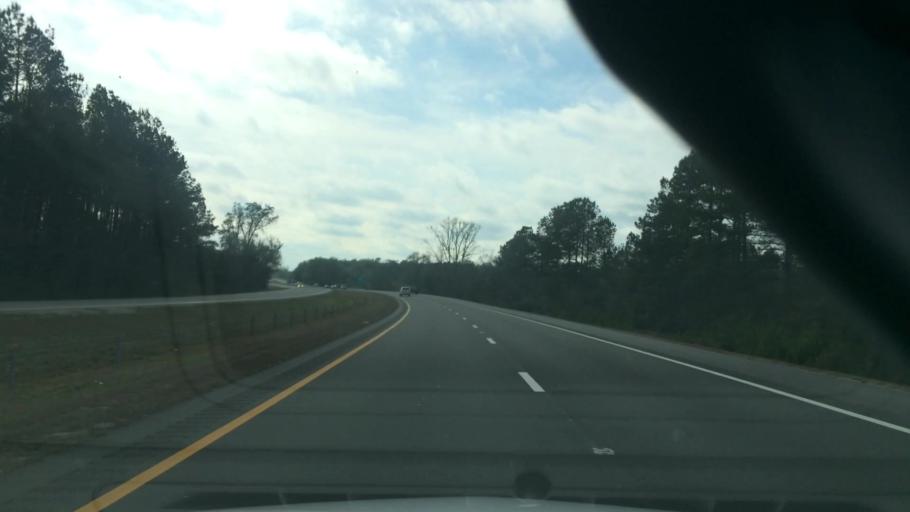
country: US
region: North Carolina
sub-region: New Hanover County
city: Wrightsboro
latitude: 34.3163
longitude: -77.9442
